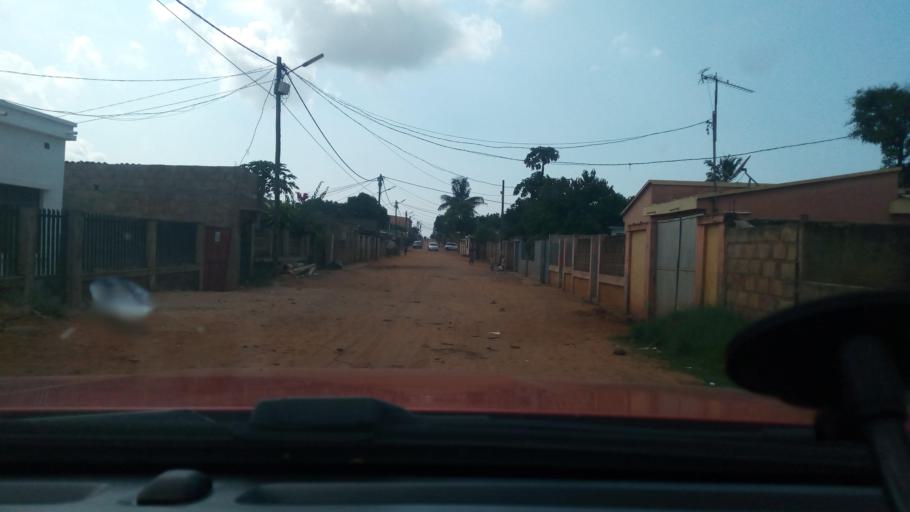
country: MZ
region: Maputo City
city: Maputo
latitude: -25.9225
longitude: 32.5907
